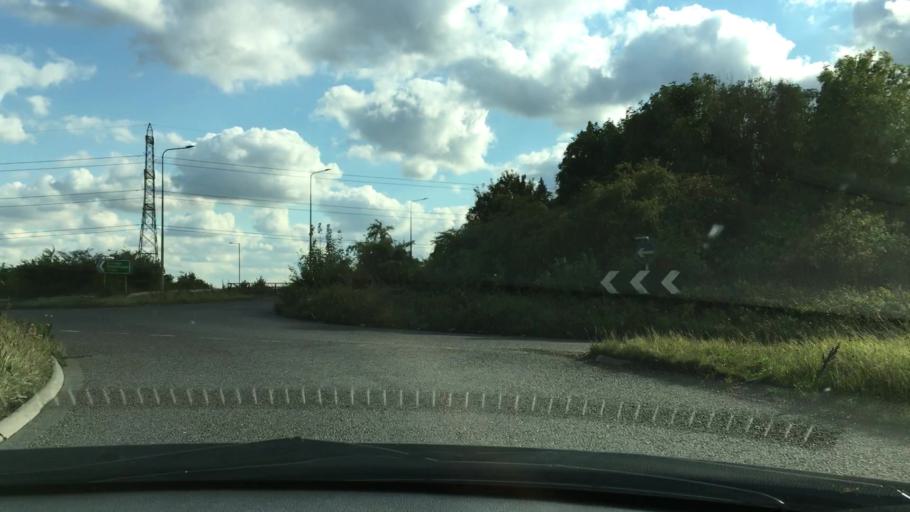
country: GB
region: England
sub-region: North East Lincolnshire
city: Immingham
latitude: 53.5983
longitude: -0.1967
